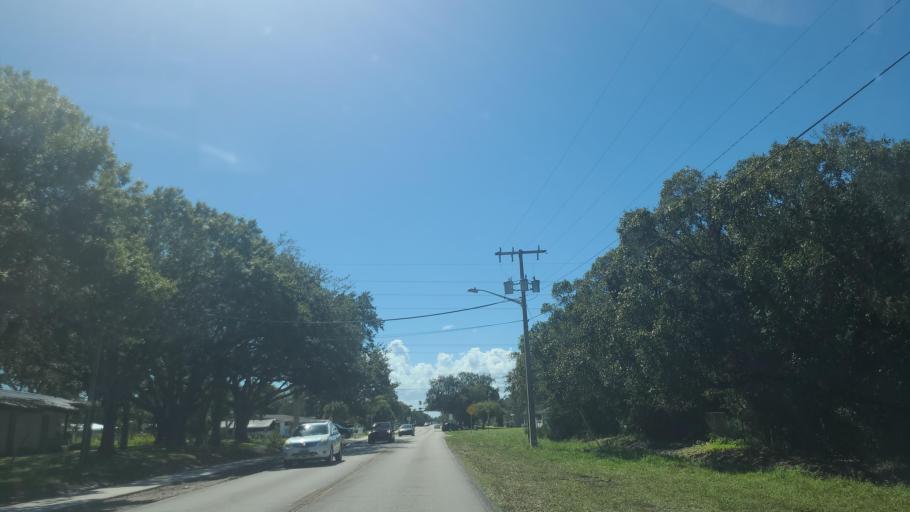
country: US
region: Florida
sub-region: Indian River County
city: Vero Beach
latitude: 27.6351
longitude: -80.3851
